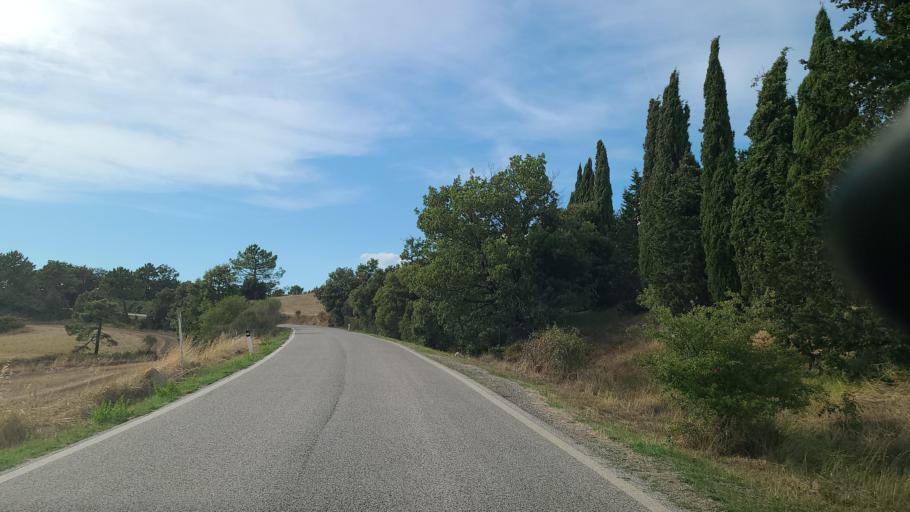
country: IT
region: Tuscany
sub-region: Provincia di Siena
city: San Gimignano
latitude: 43.4275
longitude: 10.9728
